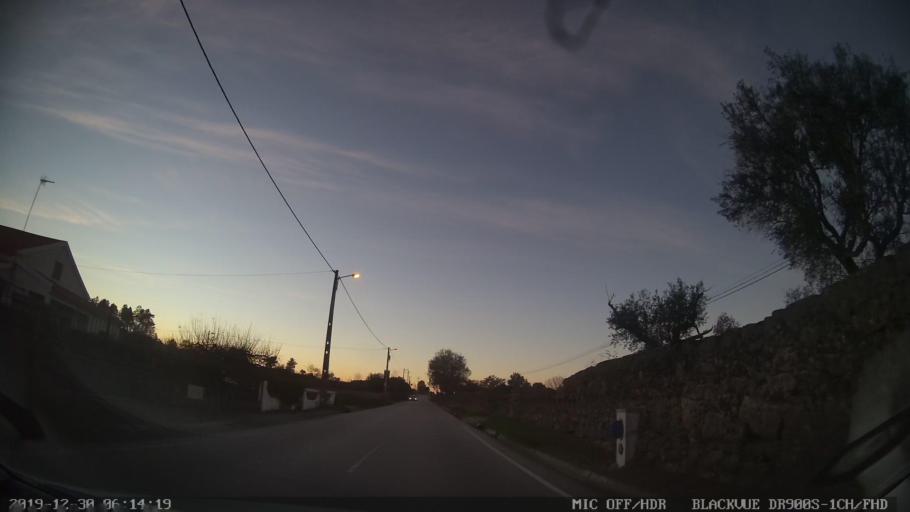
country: PT
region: Castelo Branco
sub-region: Penamacor
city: Penamacor
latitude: 40.1126
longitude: -7.2166
